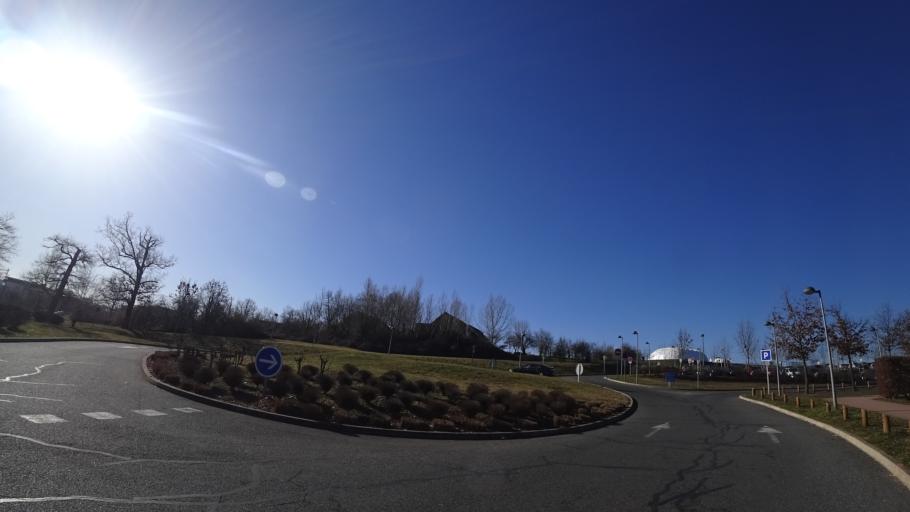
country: FR
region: Midi-Pyrenees
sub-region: Departement de l'Aveyron
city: Olemps
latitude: 44.3599
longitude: 2.5540
